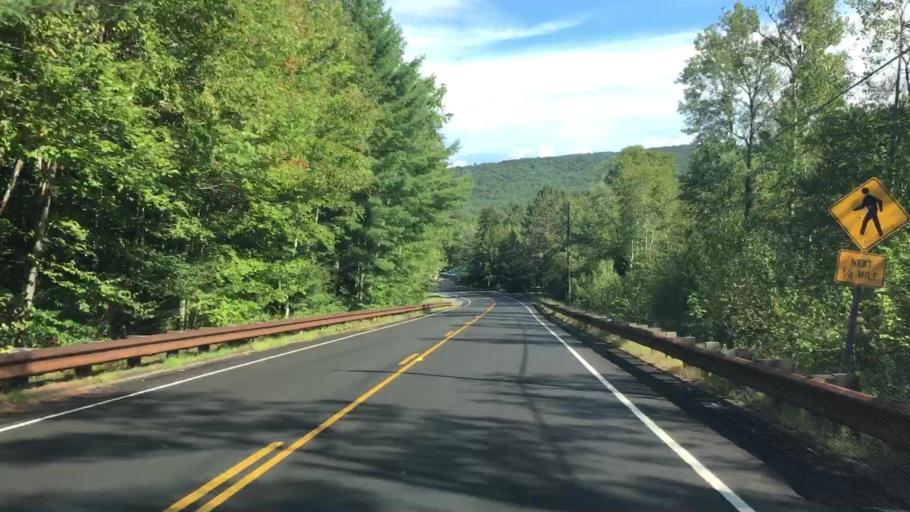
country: US
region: New Hampshire
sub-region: Grafton County
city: Woodstock
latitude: 44.0201
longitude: -71.7456
